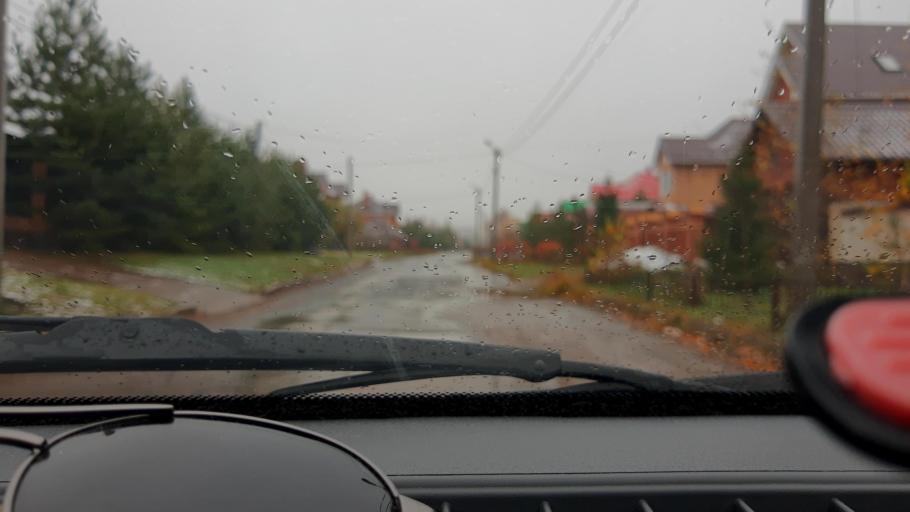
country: RU
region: Bashkortostan
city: Kabakovo
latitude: 54.6245
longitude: 56.1247
